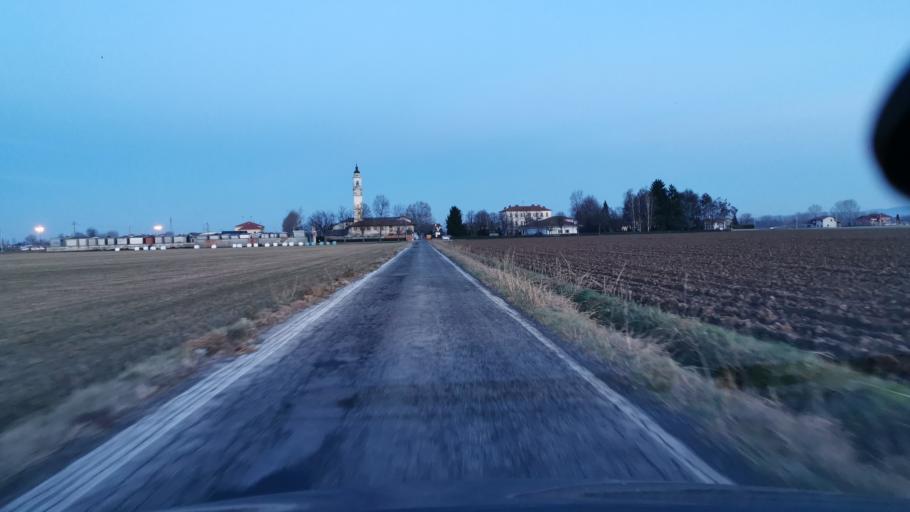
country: IT
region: Piedmont
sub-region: Provincia di Cuneo
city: Roata Rossi
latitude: 44.4529
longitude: 7.4861
